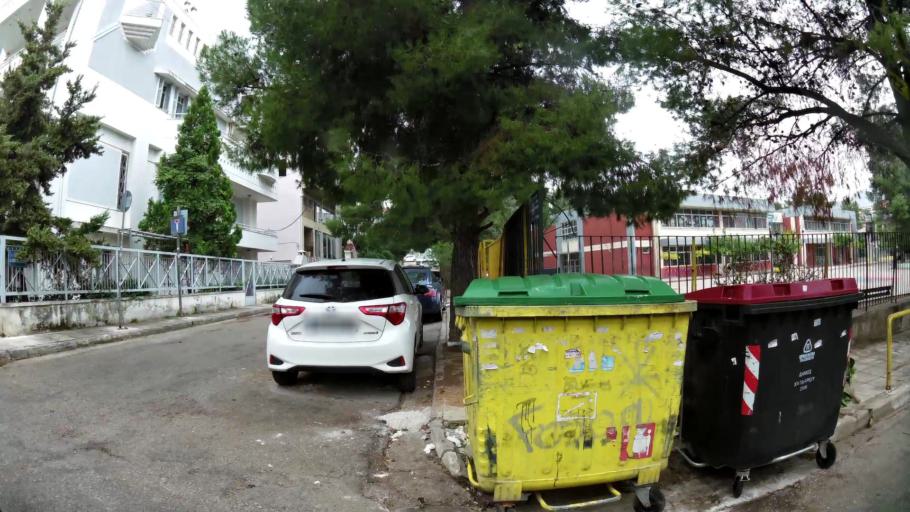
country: GR
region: Attica
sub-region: Nomarchia Athinas
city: Chaidari
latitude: 38.0094
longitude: 23.6514
